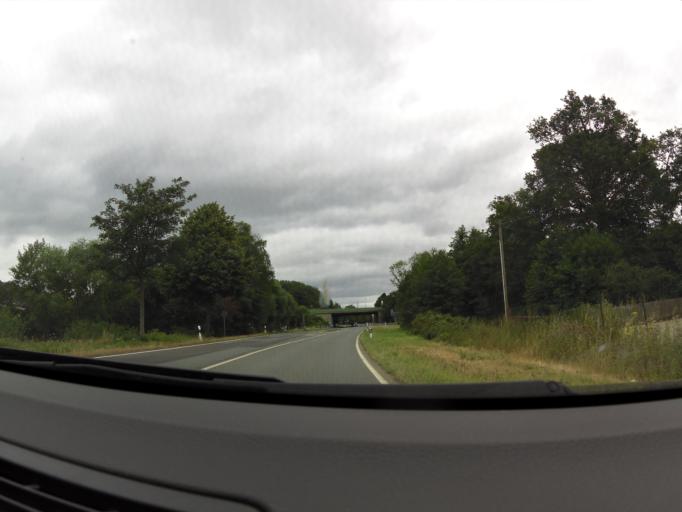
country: DE
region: North Rhine-Westphalia
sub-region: Regierungsbezirk Dusseldorf
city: Sonsbeck
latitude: 51.6025
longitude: 6.3465
